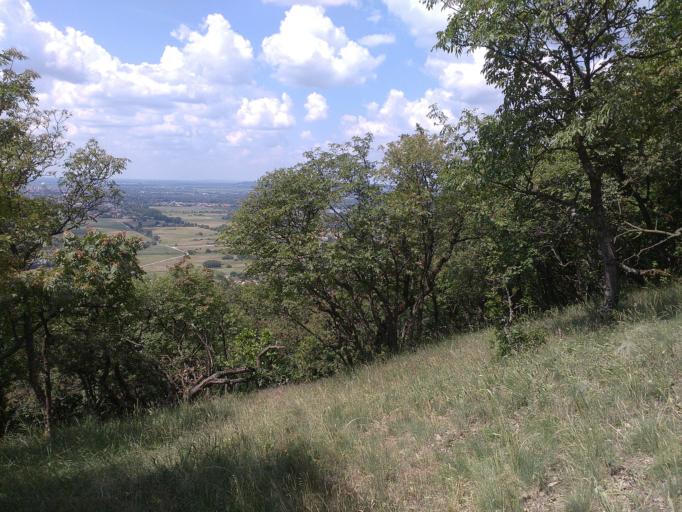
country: HU
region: Komarom-Esztergom
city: Esztergom
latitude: 47.8080
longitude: 18.7975
